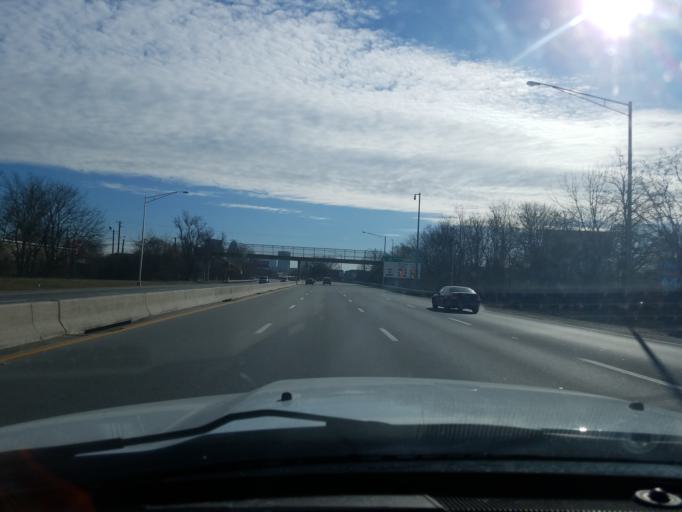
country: US
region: Kentucky
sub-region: Jefferson County
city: Louisville
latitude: 38.2671
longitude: -85.7802
